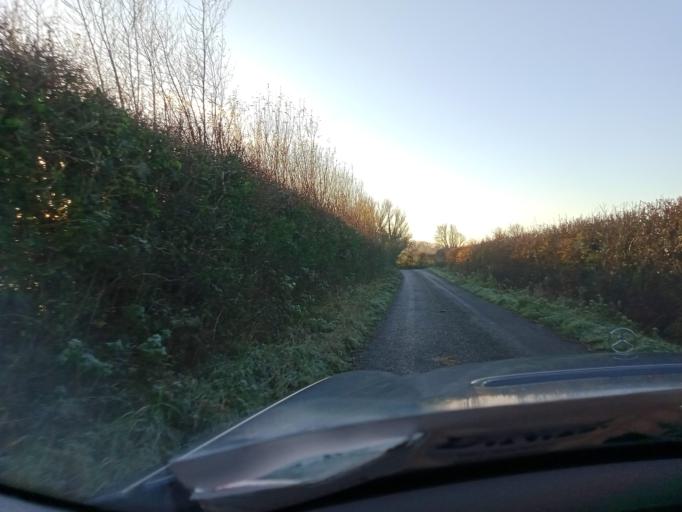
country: IE
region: Leinster
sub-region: Kilkenny
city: Callan
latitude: 52.5171
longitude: -7.4467
